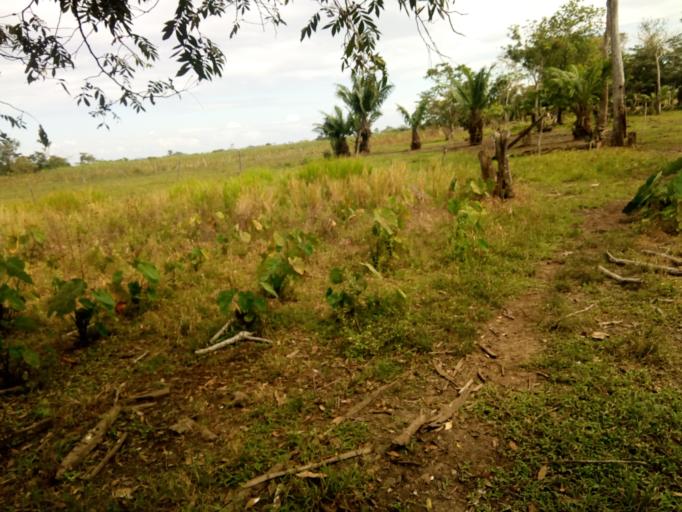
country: CR
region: Alajuela
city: San Jose
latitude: 11.0569
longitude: -85.1943
